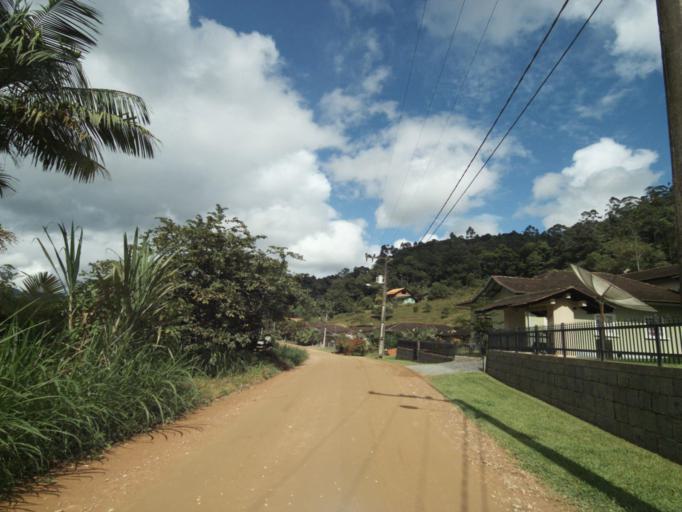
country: BR
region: Santa Catarina
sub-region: Pomerode
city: Pomerode
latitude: -26.6899
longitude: -49.1772
